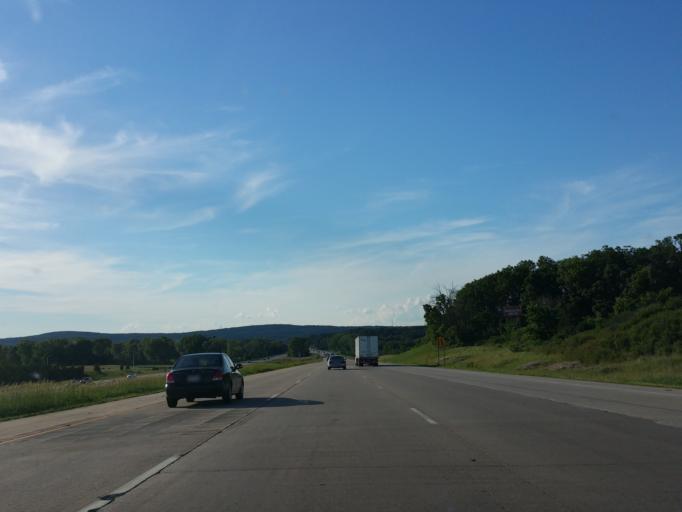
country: US
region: Wisconsin
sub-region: Columbia County
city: Poynette
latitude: 43.4300
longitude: -89.4811
